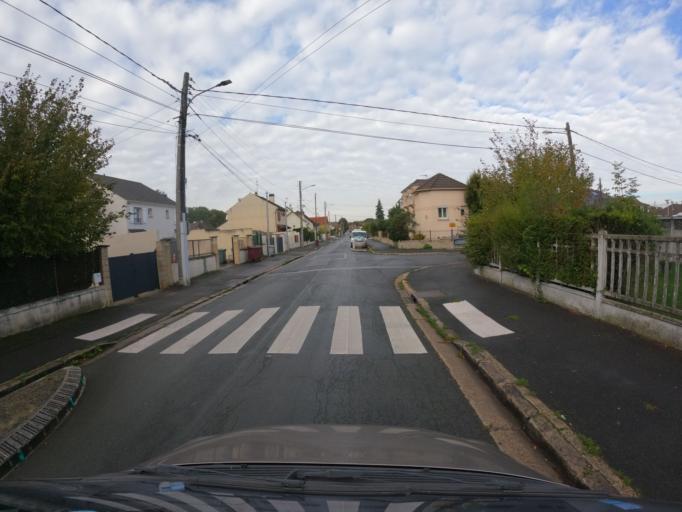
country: FR
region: Ile-de-France
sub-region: Departement de Seine-et-Marne
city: Chelles
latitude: 48.8995
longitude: 2.5988
